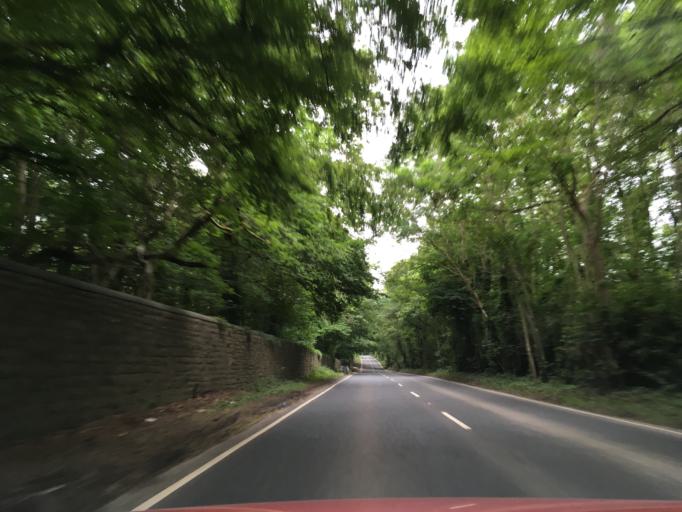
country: GB
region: England
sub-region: North Somerset
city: Long Ashton
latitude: 51.4530
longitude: -2.6502
